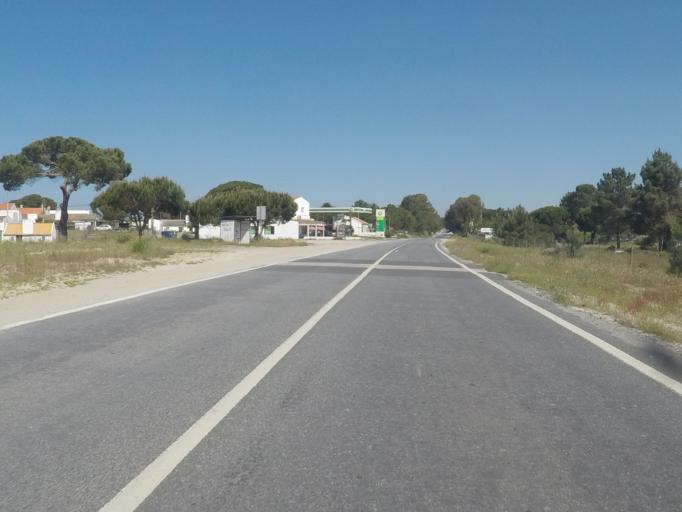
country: PT
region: Setubal
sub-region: Grandola
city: Grandola
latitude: 38.3090
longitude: -8.7420
